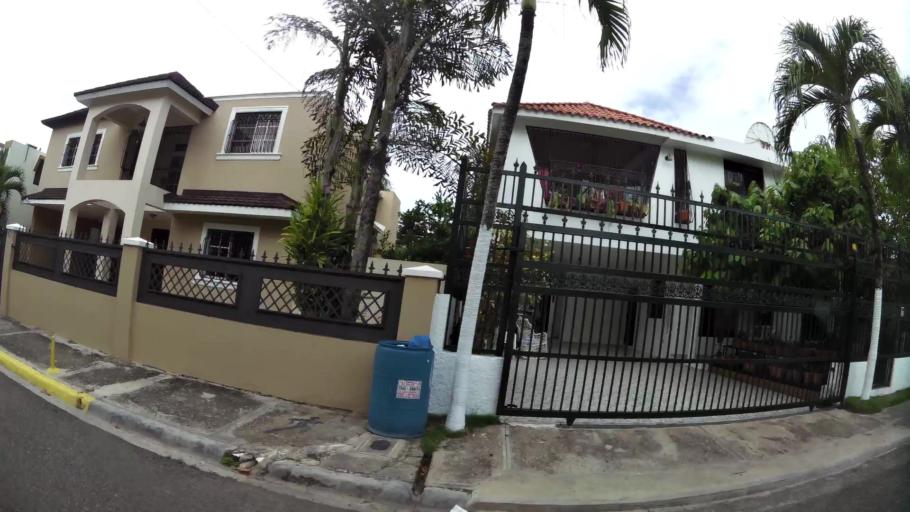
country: DO
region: Santiago
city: Santiago de los Caballeros
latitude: 19.4597
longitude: -70.6695
